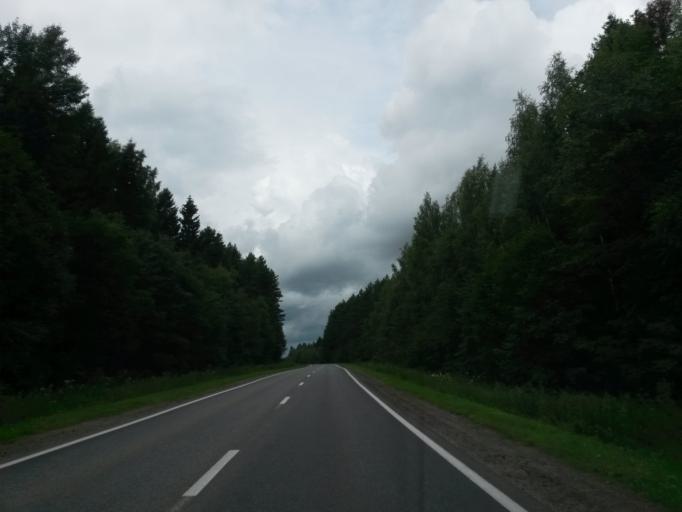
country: RU
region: Jaroslavl
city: Konstantinovskiy
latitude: 57.8232
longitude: 39.6819
